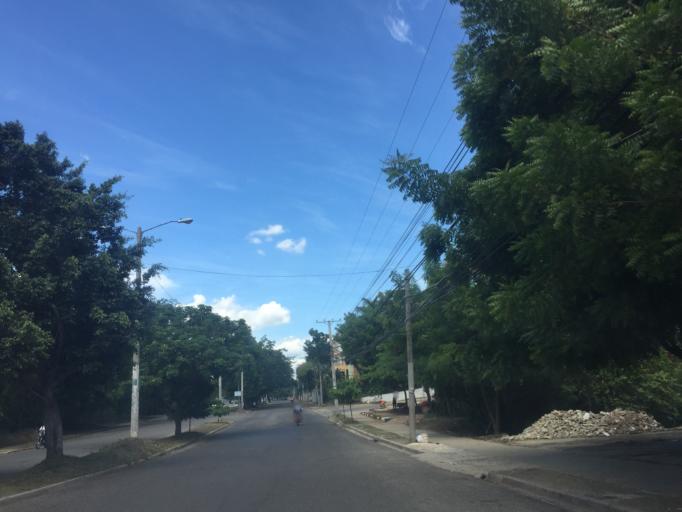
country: DO
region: Santiago
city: Santiago de los Caballeros
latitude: 19.4354
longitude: -70.6851
